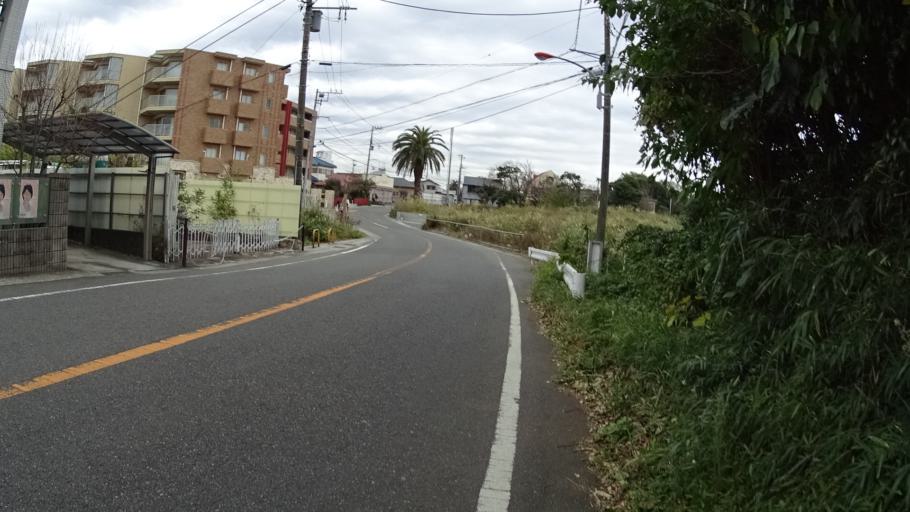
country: JP
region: Kanagawa
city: Miura
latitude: 35.1608
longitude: 139.6154
